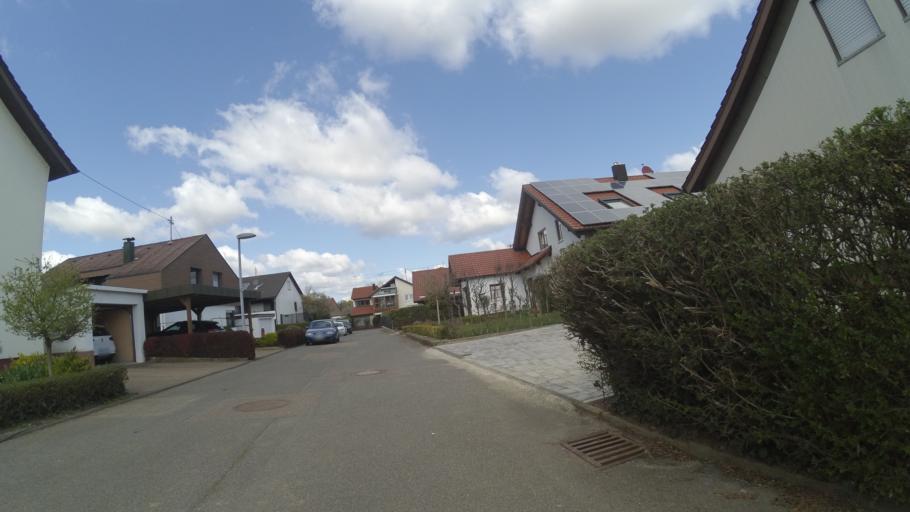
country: DE
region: Baden-Wuerttemberg
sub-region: Regierungsbezirk Stuttgart
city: Oedheim
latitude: 49.2478
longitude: 9.2879
